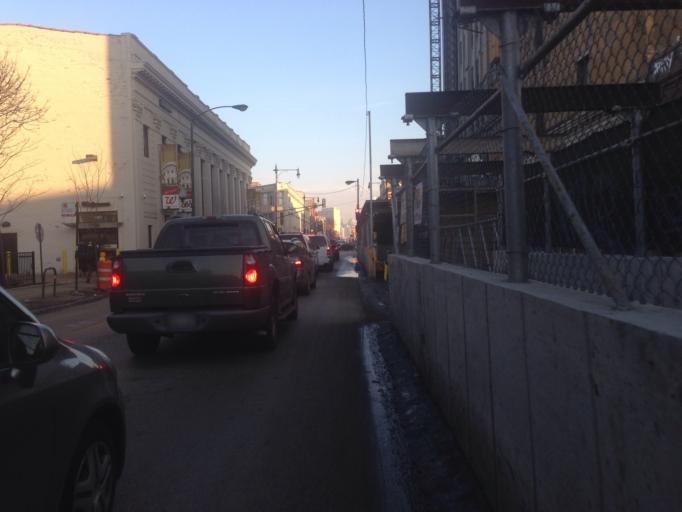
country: US
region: Illinois
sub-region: Cook County
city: Chicago
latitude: 41.9110
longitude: -87.6785
